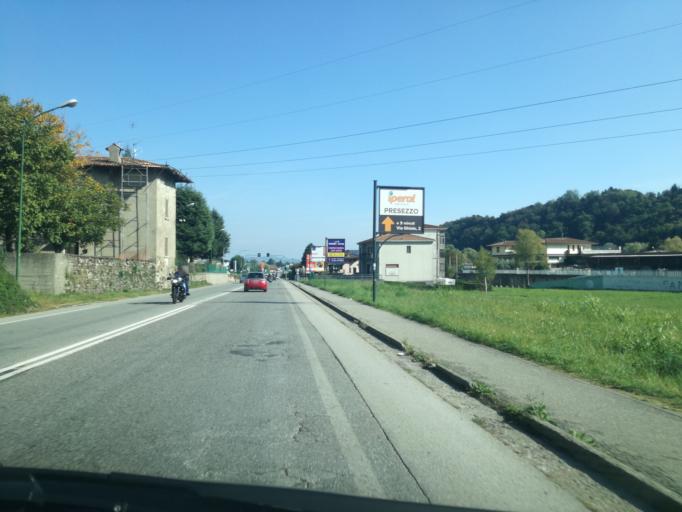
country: IT
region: Lombardy
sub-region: Provincia di Bergamo
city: Pontida
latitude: 45.7312
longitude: 9.5092
